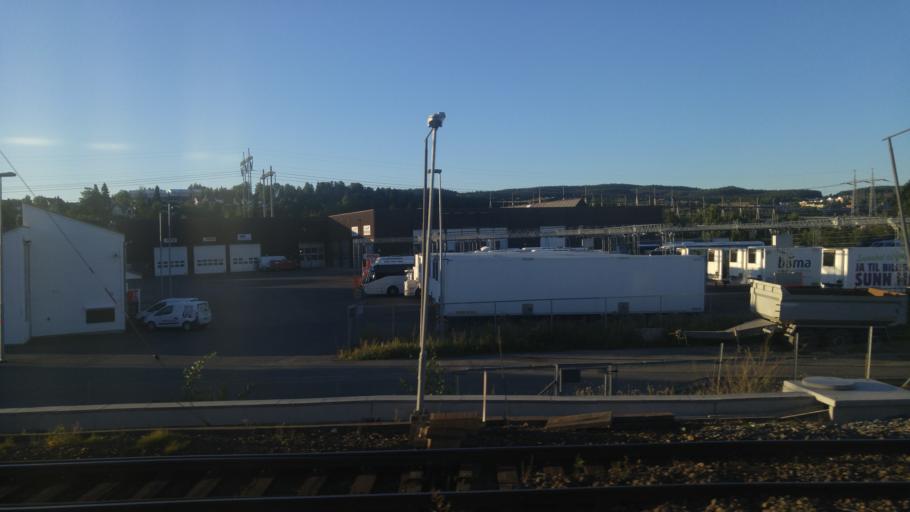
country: NO
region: Akershus
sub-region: Lorenskog
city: Kjenn
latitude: 59.9475
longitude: 10.8824
